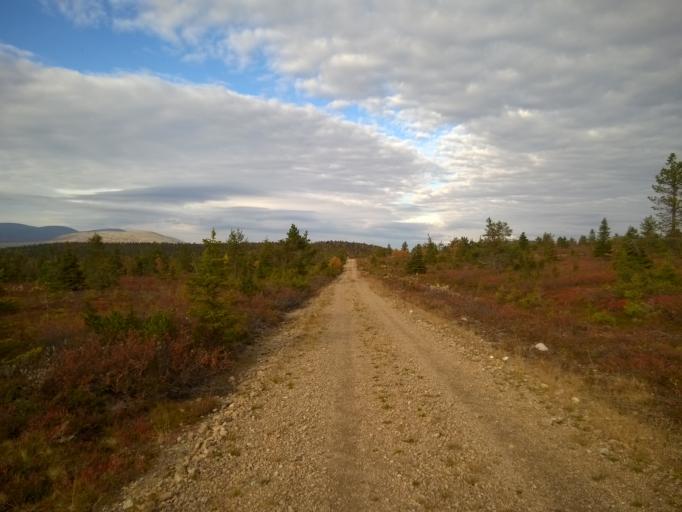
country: FI
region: Lapland
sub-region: Tunturi-Lappi
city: Muonio
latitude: 67.9761
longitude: 24.1023
